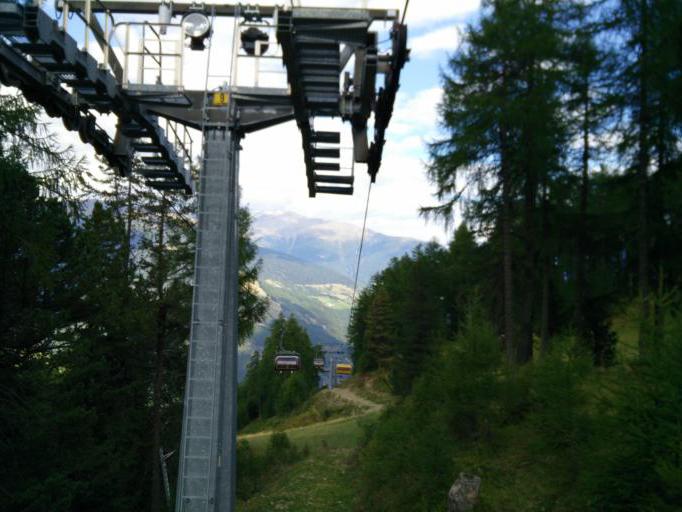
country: IT
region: Trentino-Alto Adige
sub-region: Bolzano
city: Malles Venosta
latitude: 46.7056
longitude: 10.5016
